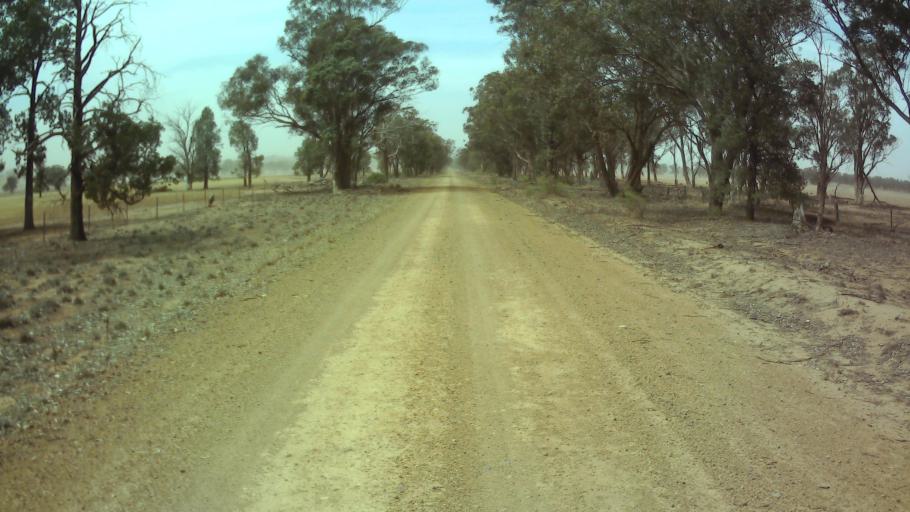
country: AU
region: New South Wales
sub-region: Weddin
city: Grenfell
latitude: -33.7324
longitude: 147.9626
